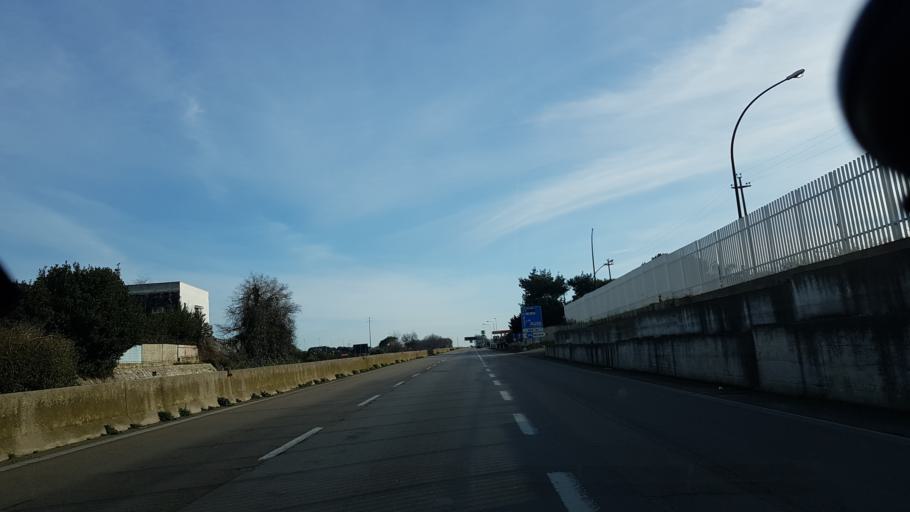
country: IT
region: Apulia
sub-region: Provincia di Brindisi
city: Brindisi
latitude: 40.6353
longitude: 17.9165
